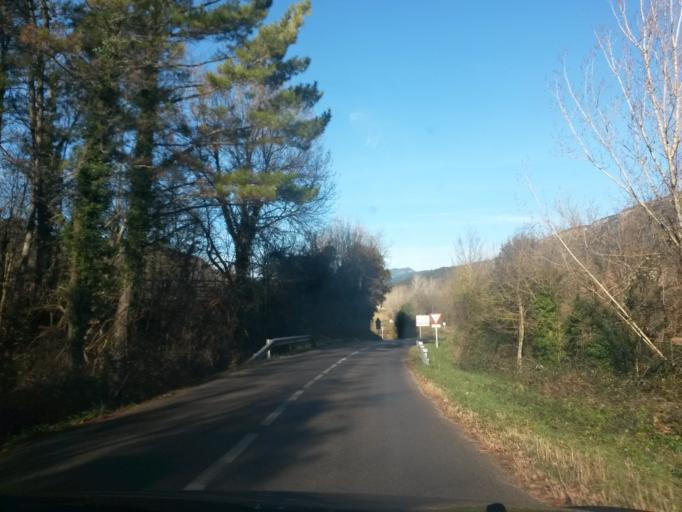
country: ES
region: Catalonia
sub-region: Provincia de Girona
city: la Cellera de Ter
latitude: 42.0259
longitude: 2.6635
